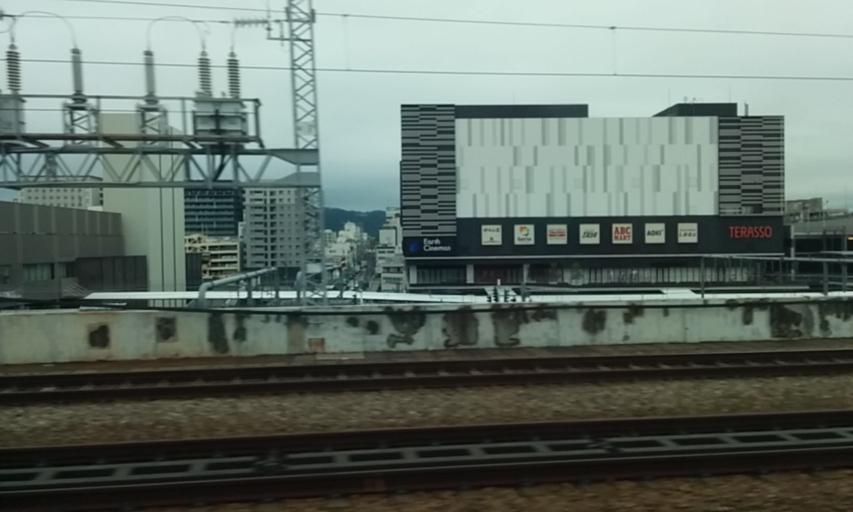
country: JP
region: Hyogo
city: Himeji
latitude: 34.8261
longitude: 134.6931
